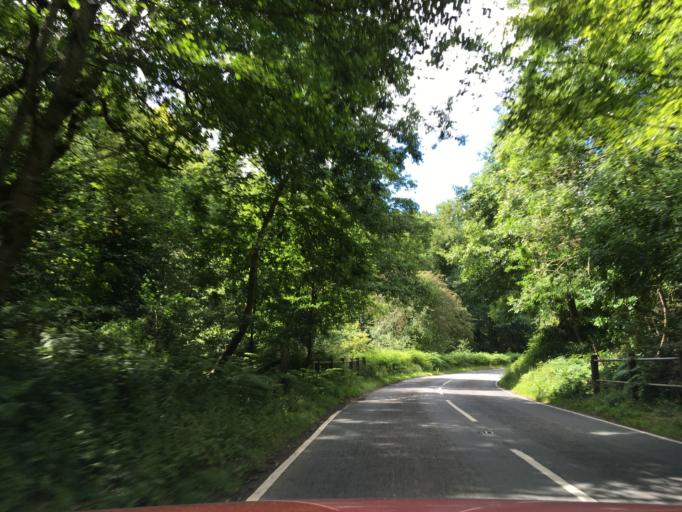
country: GB
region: England
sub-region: Gloucestershire
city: Lydney
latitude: 51.7757
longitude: -2.5174
